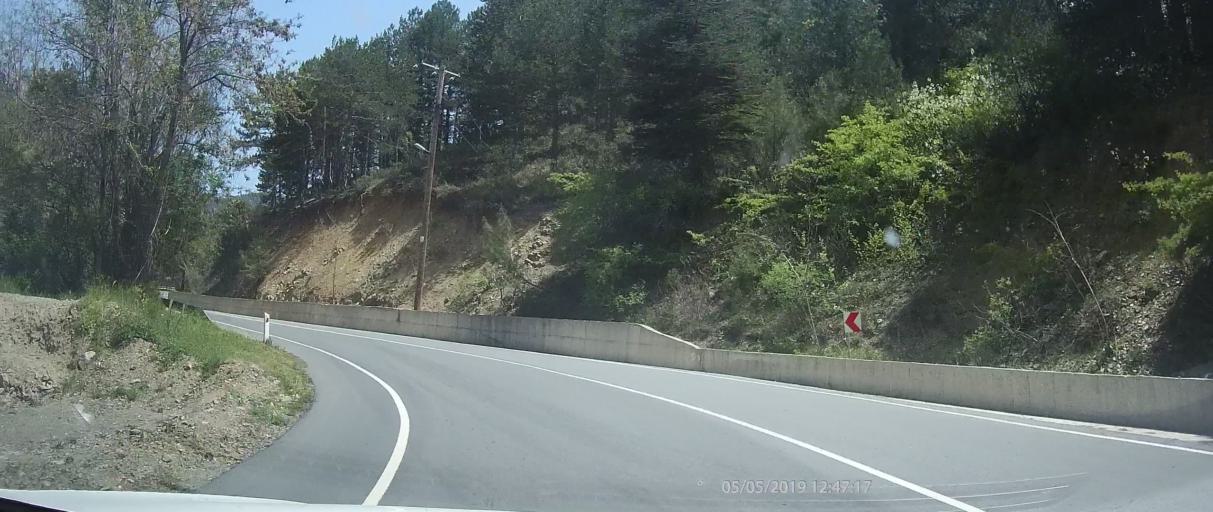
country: CY
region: Lefkosia
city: Kakopetria
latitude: 34.9597
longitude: 32.8273
